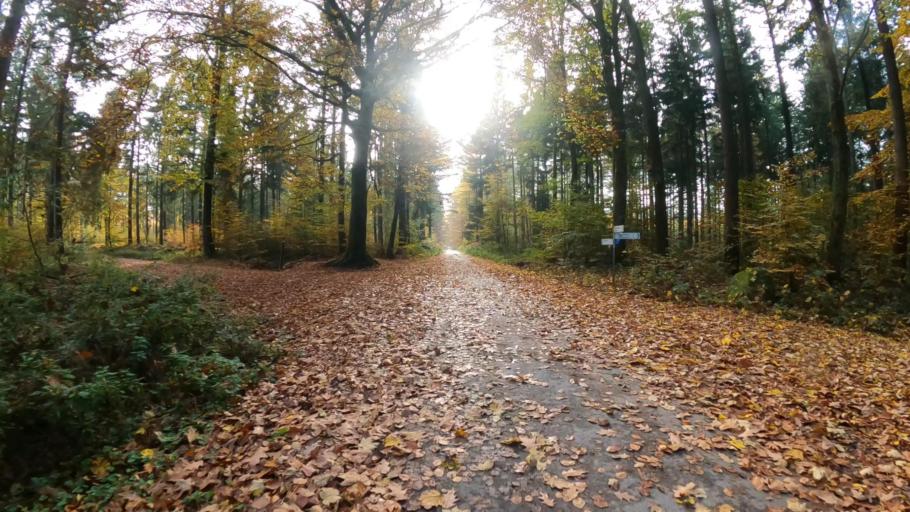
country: DE
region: Lower Saxony
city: Neu Wulmstorf
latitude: 53.3970
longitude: 9.8346
